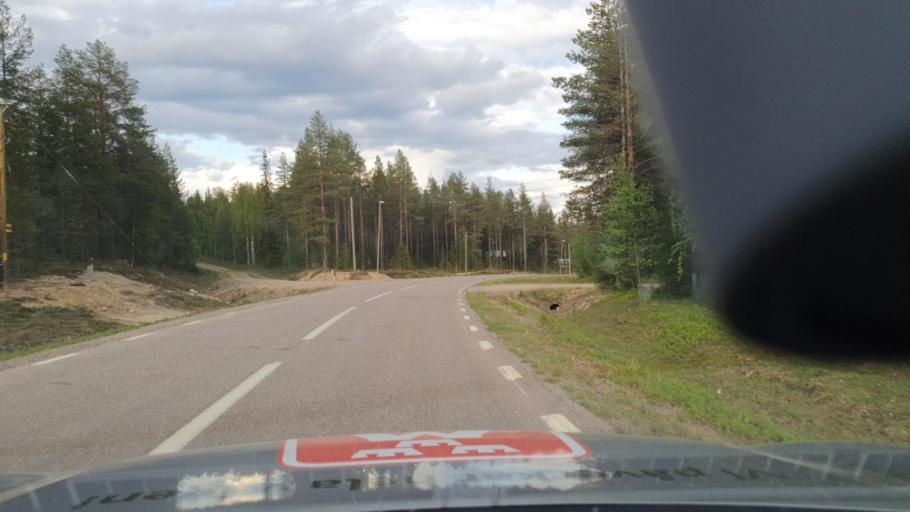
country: SE
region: Norrbotten
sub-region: Gallivare Kommun
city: Gaellivare
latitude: 66.9334
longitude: 21.2665
